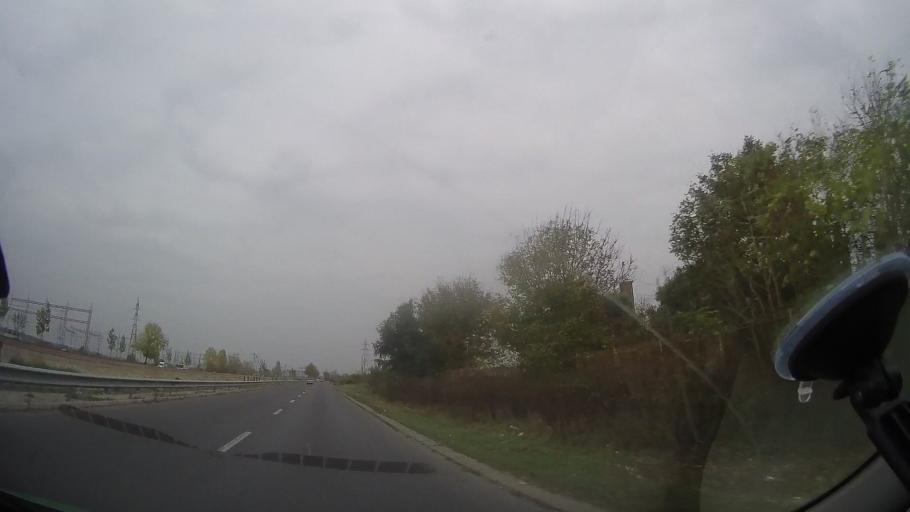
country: RO
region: Ilfov
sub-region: Comuna Popesti-Leordeni
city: Popesti-Leordeni
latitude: 44.3960
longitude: 26.1711
